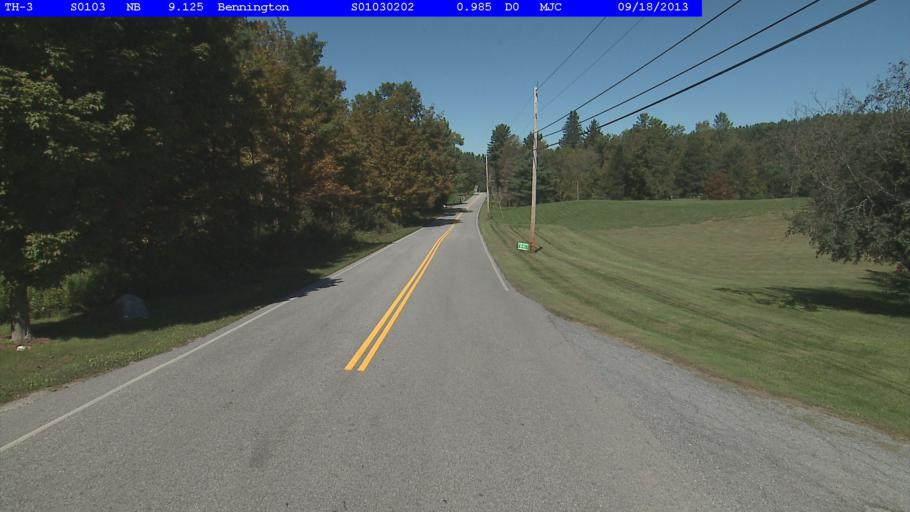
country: US
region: Vermont
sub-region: Bennington County
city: Bennington
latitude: 42.8508
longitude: -73.1729
